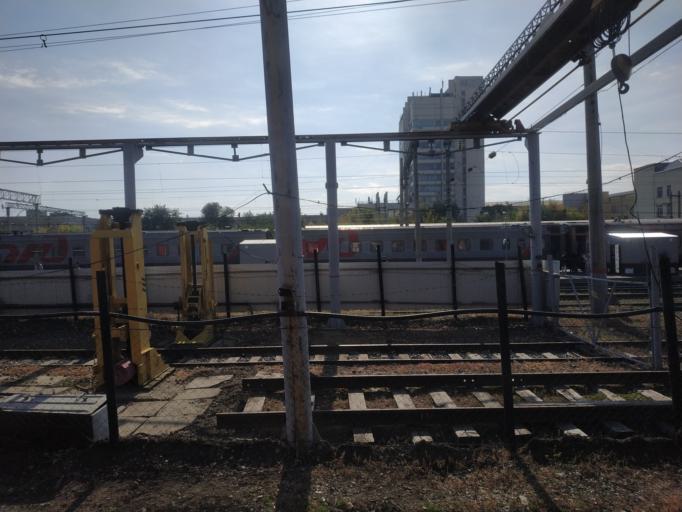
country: RU
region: Volgograd
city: Volgograd
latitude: 48.7145
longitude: 44.5154
